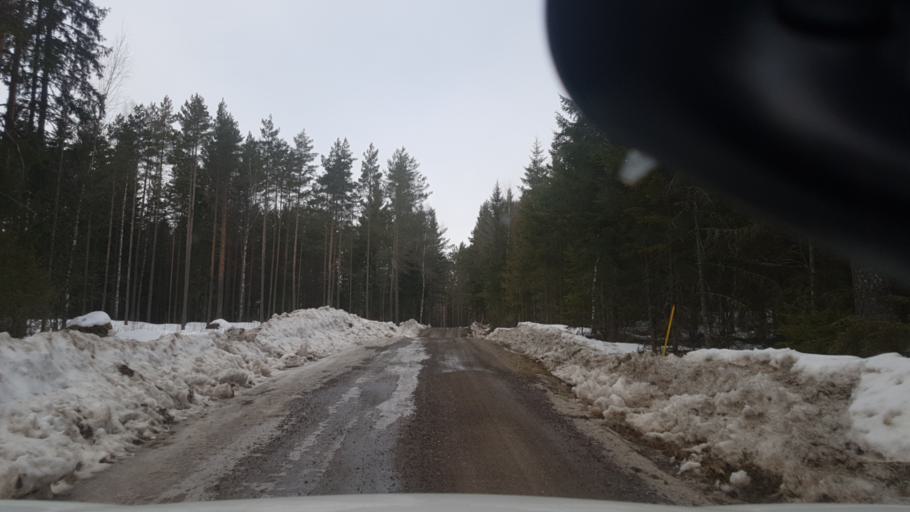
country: SE
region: Vaermland
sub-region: Eda Kommun
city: Amotfors
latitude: 59.8305
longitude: 12.3899
